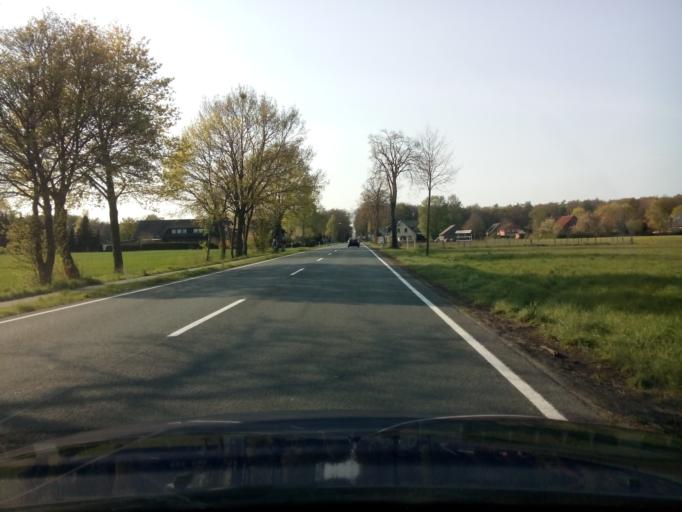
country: DE
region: Lower Saxony
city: Syke
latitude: 52.9563
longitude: 8.8067
